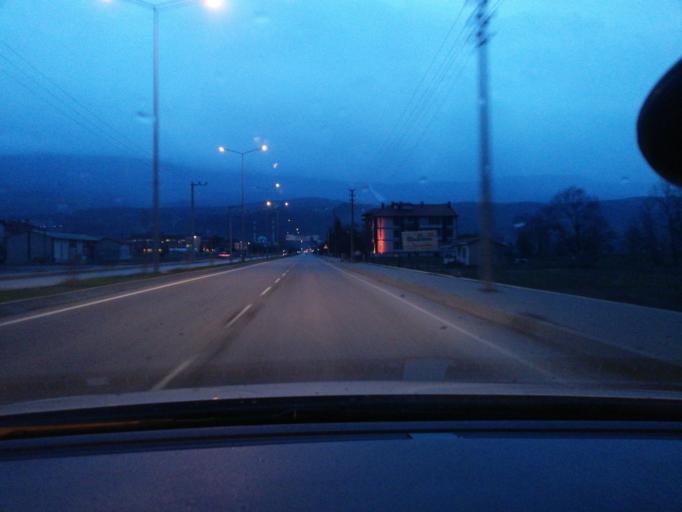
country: TR
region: Bolu
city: Bolu
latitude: 40.6952
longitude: 31.6191
